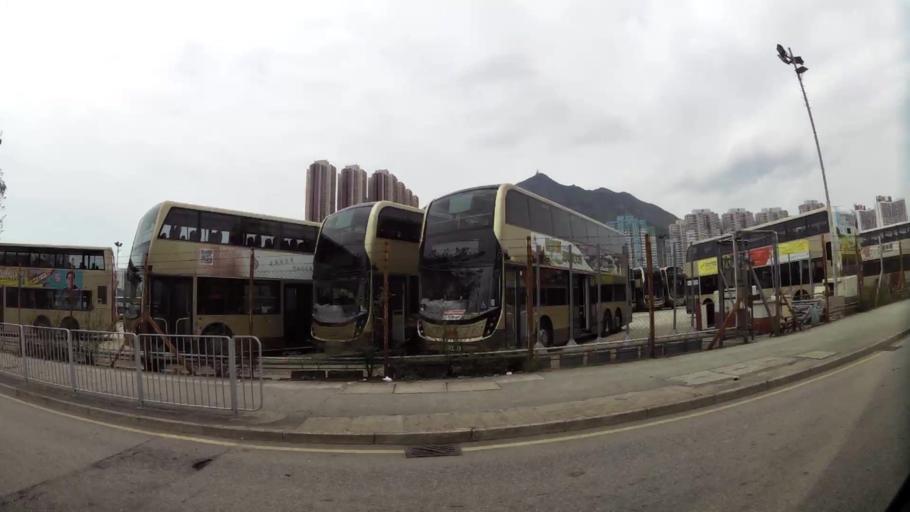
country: HK
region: Tuen Mun
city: Tuen Mun
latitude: 22.3813
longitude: 113.9701
